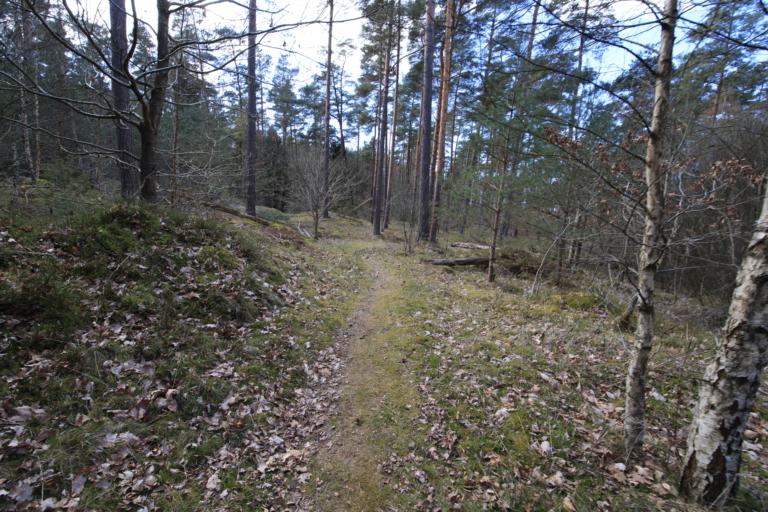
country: SE
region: Halland
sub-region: Varbergs Kommun
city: Varberg
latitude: 57.1829
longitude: 12.2322
